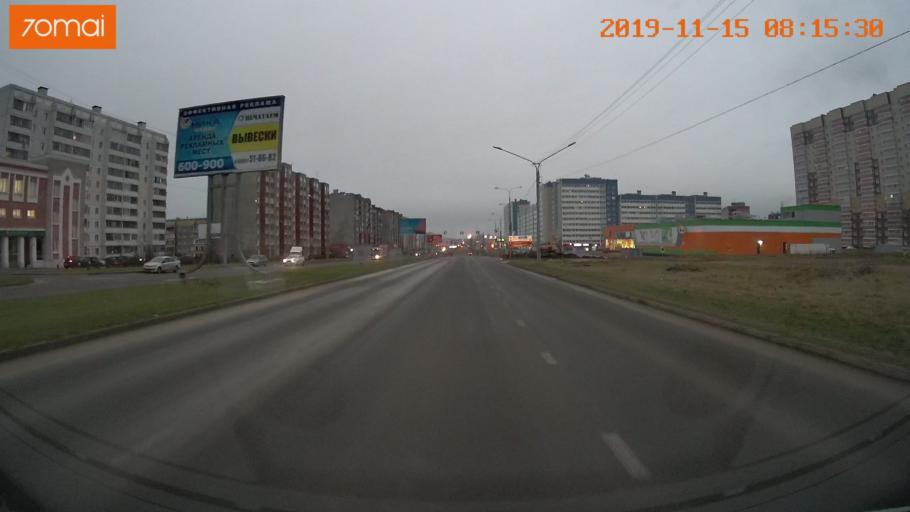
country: RU
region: Vologda
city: Cherepovets
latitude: 59.0829
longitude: 37.9219
